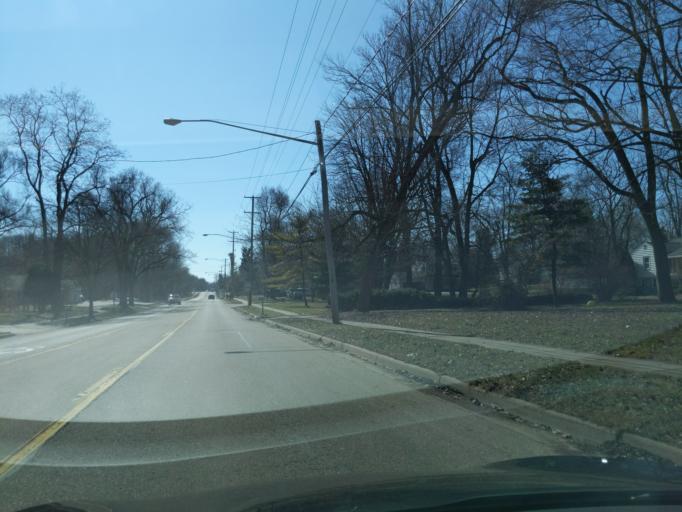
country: US
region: Michigan
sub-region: Ingham County
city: Lansing
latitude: 42.6746
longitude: -84.5629
